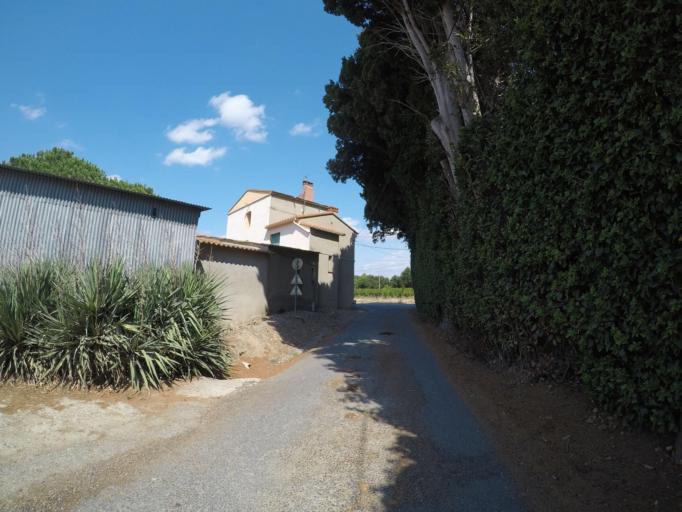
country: FR
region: Languedoc-Roussillon
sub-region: Departement des Pyrenees-Orientales
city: Saint-Esteve
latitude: 42.7032
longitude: 2.8599
